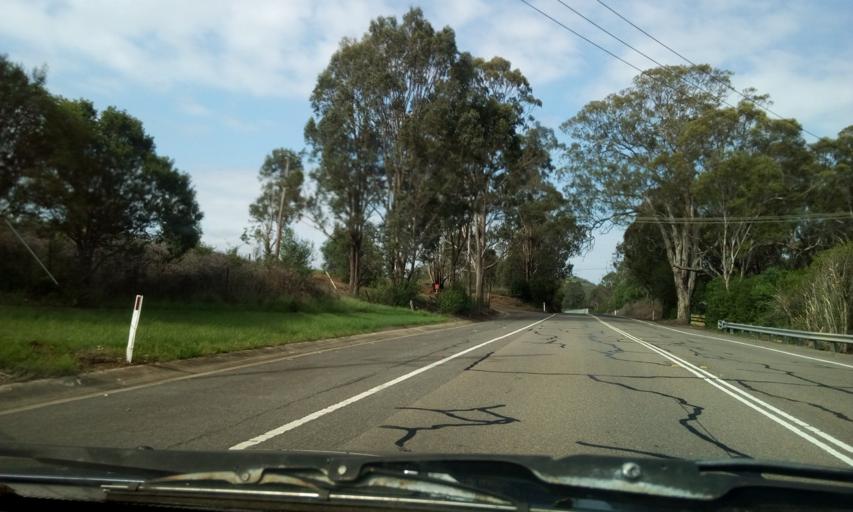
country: AU
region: New South Wales
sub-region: Campbelltown Municipality
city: Glen Alpine
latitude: -34.1082
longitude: 150.7583
